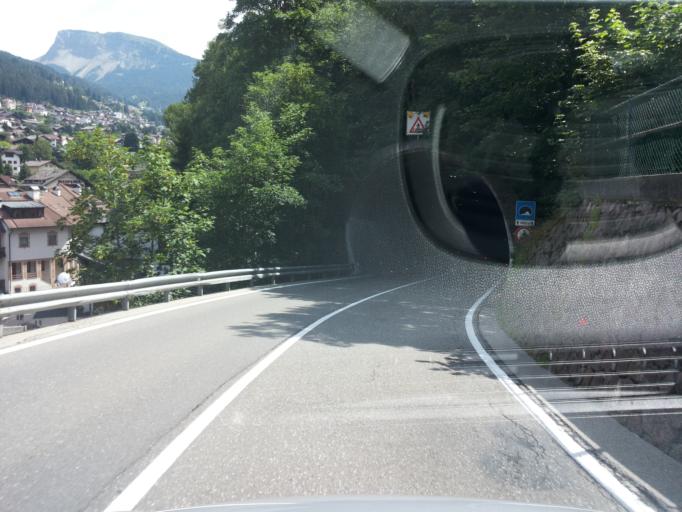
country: IT
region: Trentino-Alto Adige
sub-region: Bolzano
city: Ortisei
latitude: 46.5732
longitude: 11.6590
